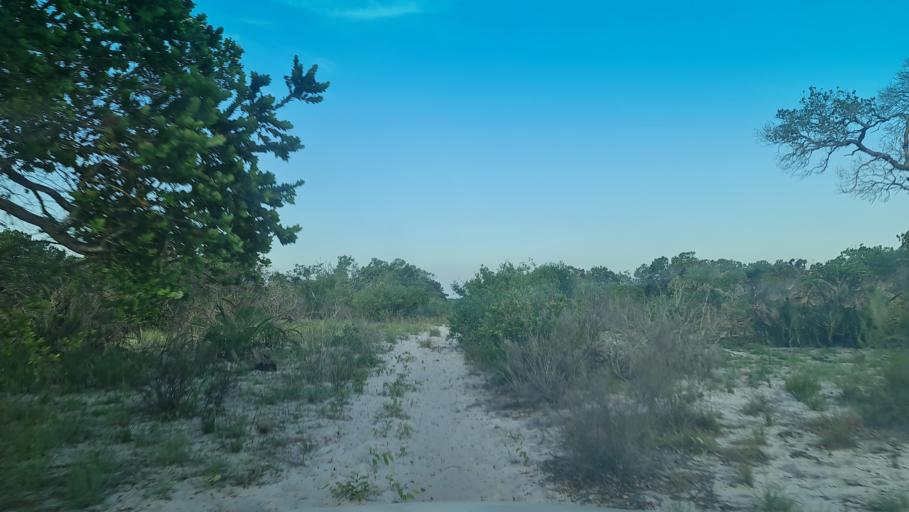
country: MZ
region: Gaza
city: Macia
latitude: -25.2150
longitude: 33.0520
